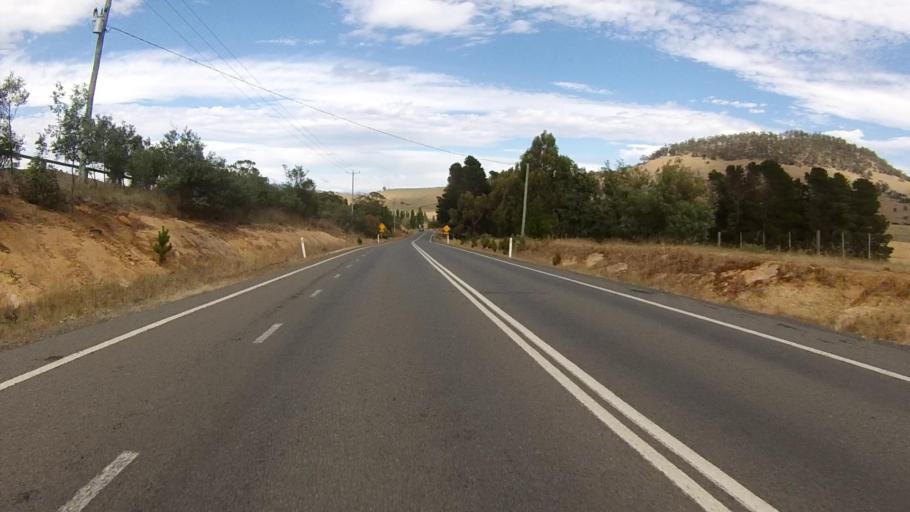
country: AU
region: Tasmania
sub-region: Brighton
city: Old Beach
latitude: -42.6704
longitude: 147.3662
